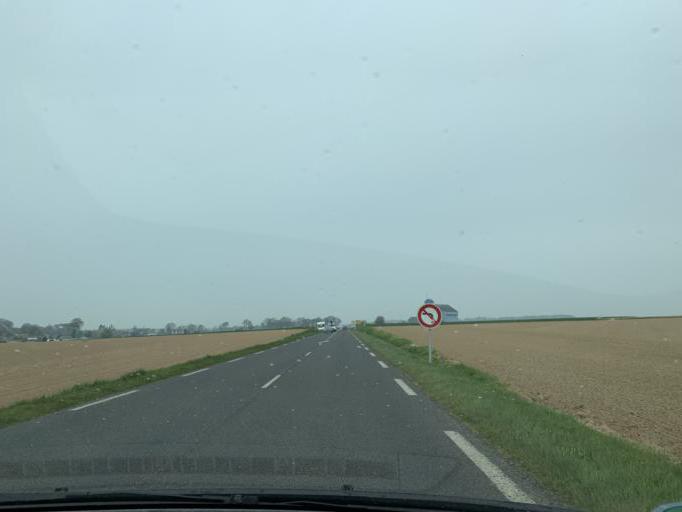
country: FR
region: Haute-Normandie
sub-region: Departement de la Seine-Maritime
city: Neville
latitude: 49.8142
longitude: 0.6701
